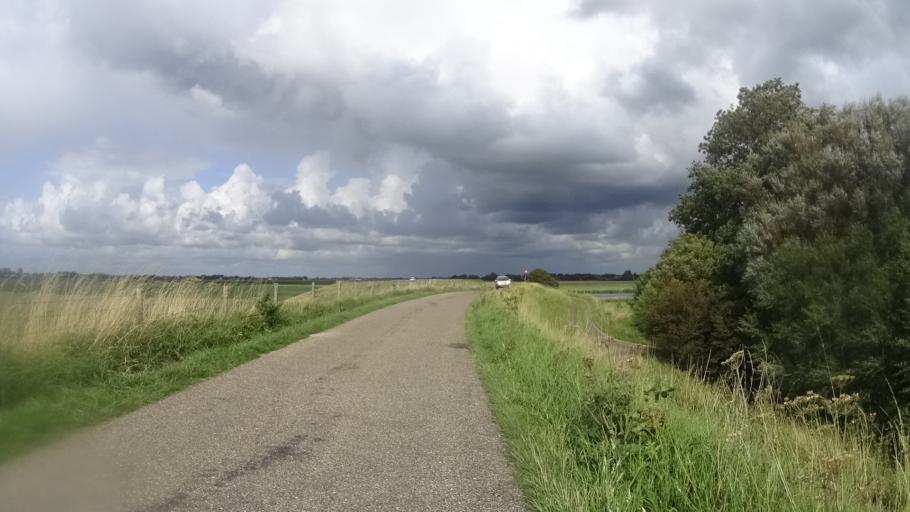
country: NL
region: North Holland
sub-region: Gemeente Schagen
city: Harenkarspel
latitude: 52.7628
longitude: 4.7276
